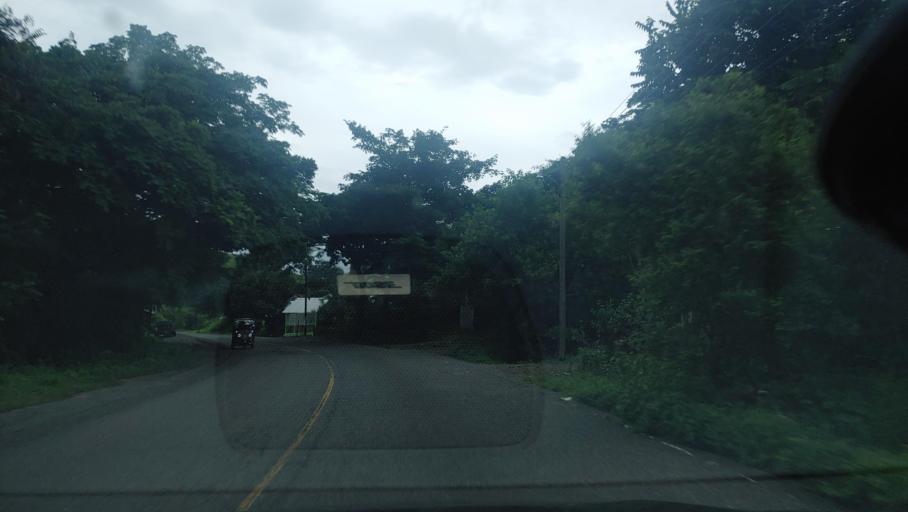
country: HN
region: Choluteca
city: Corpus
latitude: 13.3679
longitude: -87.0026
